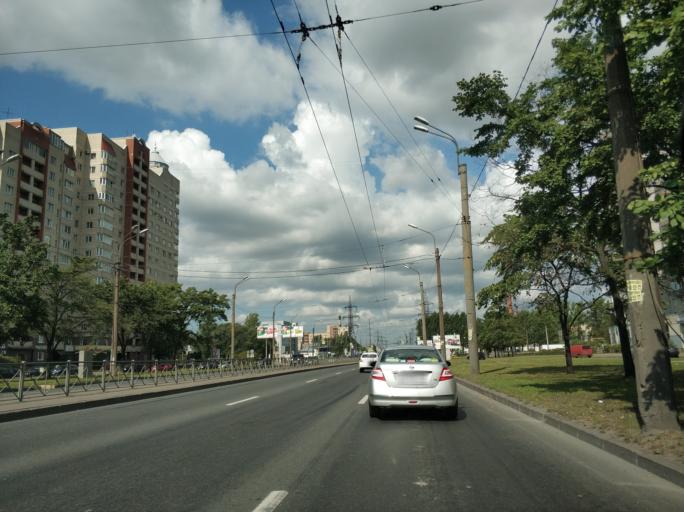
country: RU
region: St.-Petersburg
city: Krasnogvargeisky
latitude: 59.9543
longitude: 30.4687
